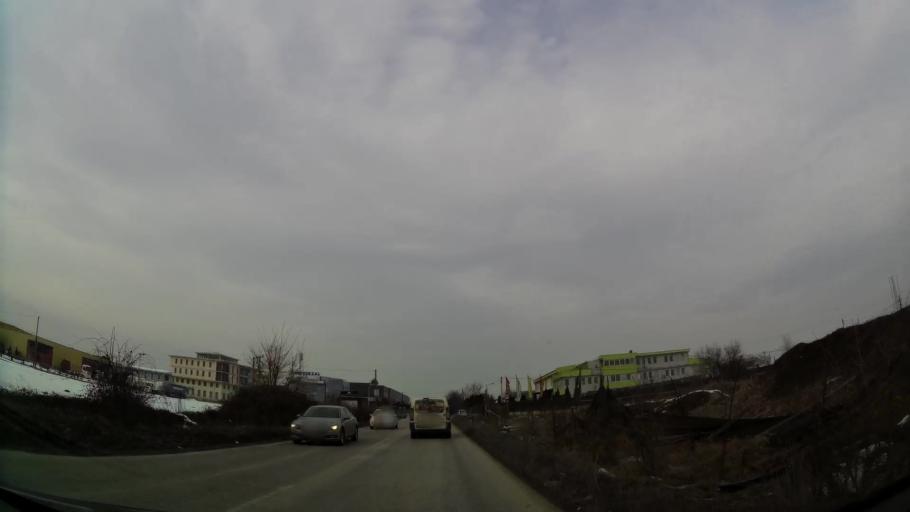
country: MK
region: Suto Orizari
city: Suto Orizare
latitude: 42.0334
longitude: 21.4022
